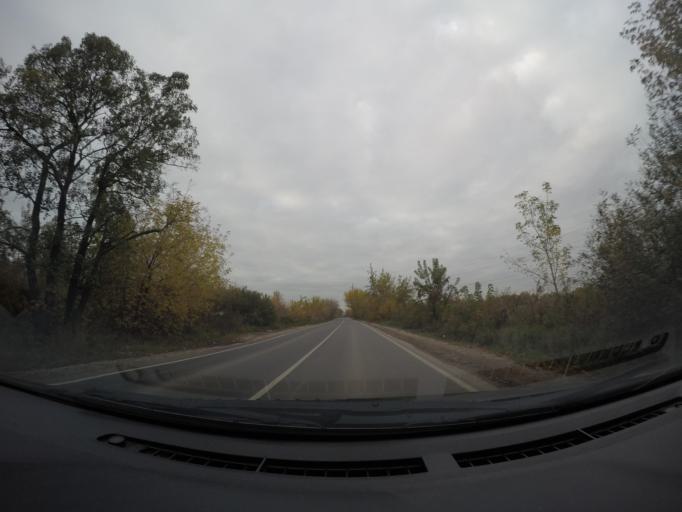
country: RU
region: Moskovskaya
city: Staraya Kupavna
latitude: 55.7839
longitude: 38.1876
